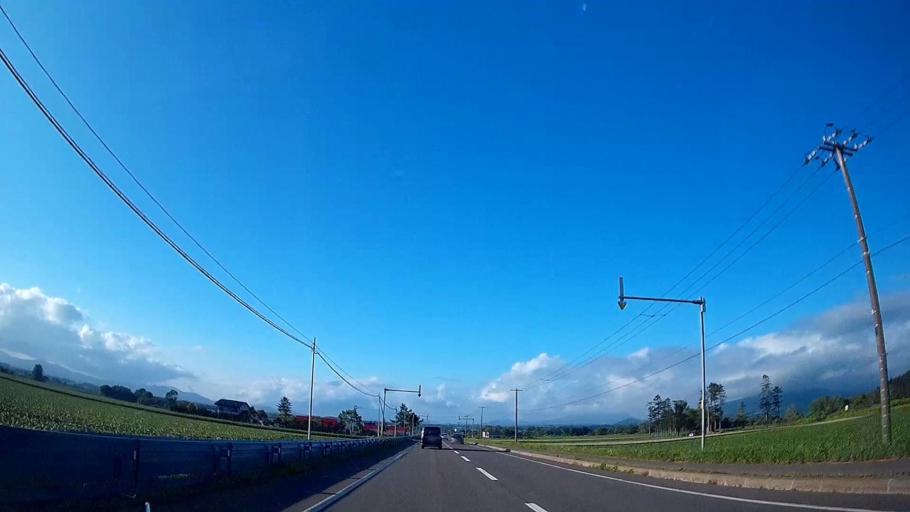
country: JP
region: Hokkaido
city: Date
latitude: 42.6355
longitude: 140.8014
